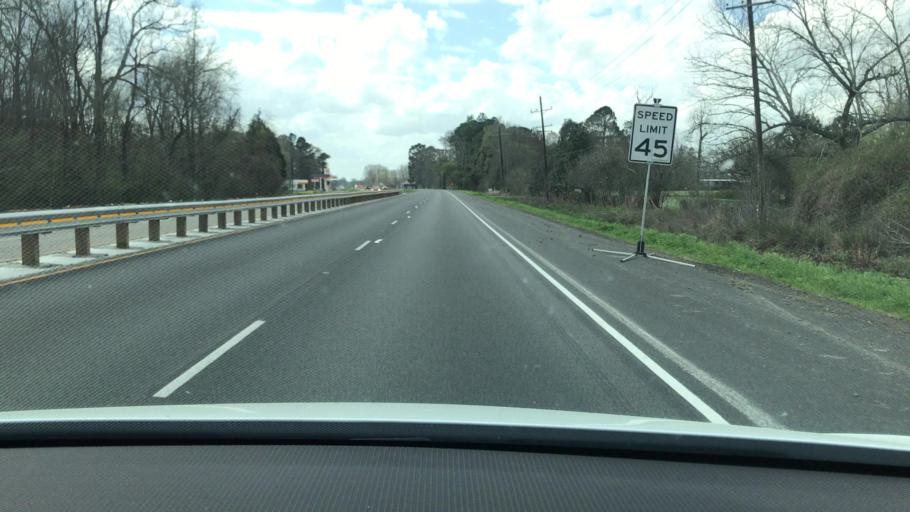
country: US
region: Louisiana
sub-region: Pointe Coupee Parish
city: Livonia
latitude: 30.5570
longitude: -91.6347
